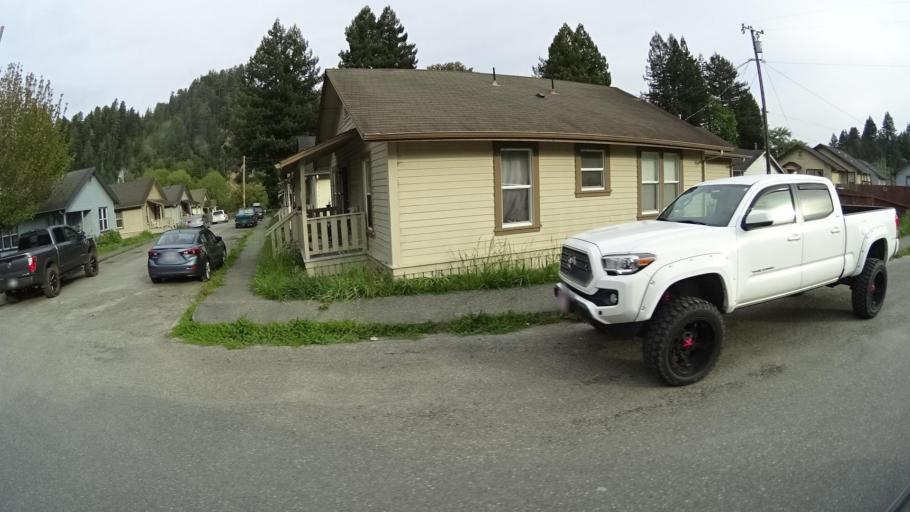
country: US
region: California
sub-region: Humboldt County
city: Rio Dell
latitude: 40.4822
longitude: -124.1065
